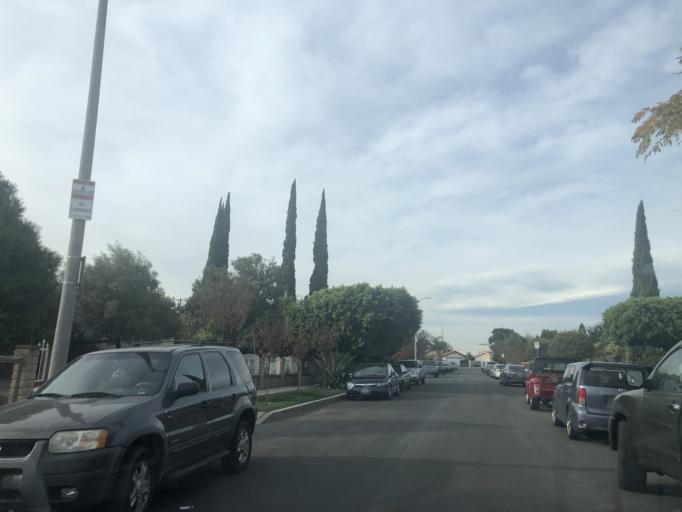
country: US
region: California
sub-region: Los Angeles County
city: San Fernando
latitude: 34.2726
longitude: -118.4338
